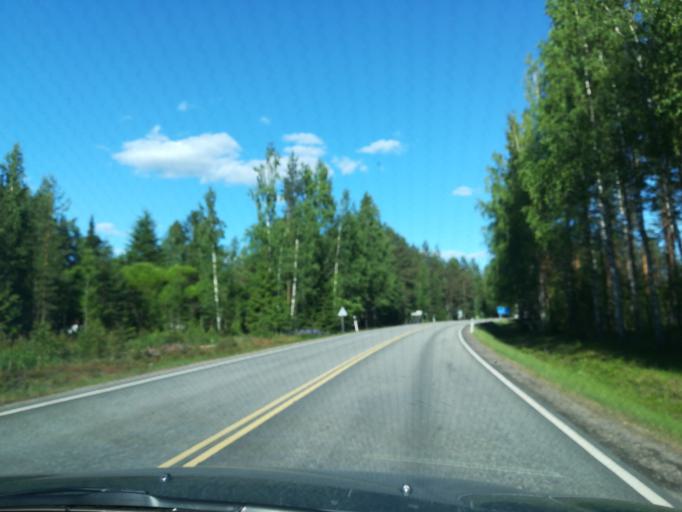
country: FI
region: South Karelia
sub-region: Imatra
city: Ruokolahti
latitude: 61.3994
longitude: 28.6216
